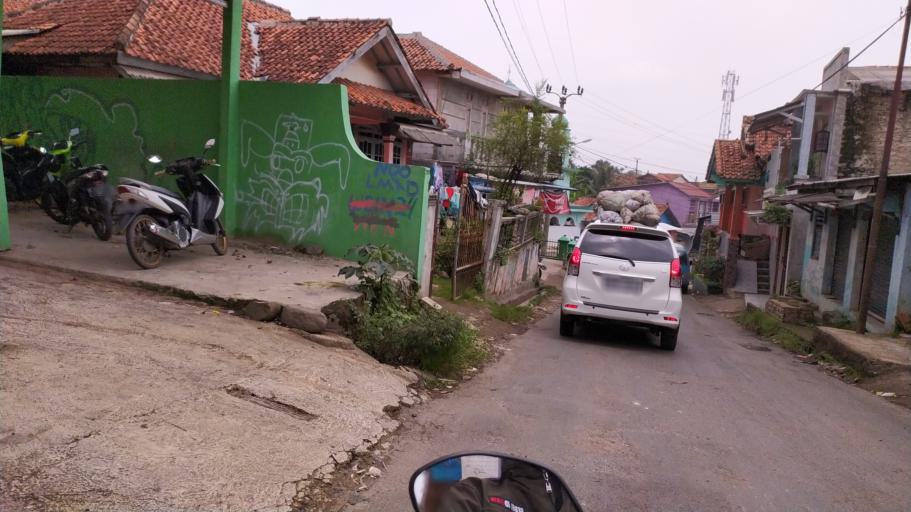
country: ID
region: West Java
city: Ciampea
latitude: -6.5919
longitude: 106.7039
